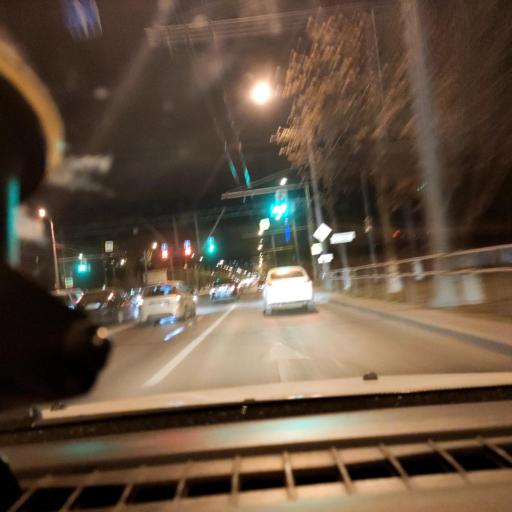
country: RU
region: Samara
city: Samara
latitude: 53.2409
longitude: 50.2070
